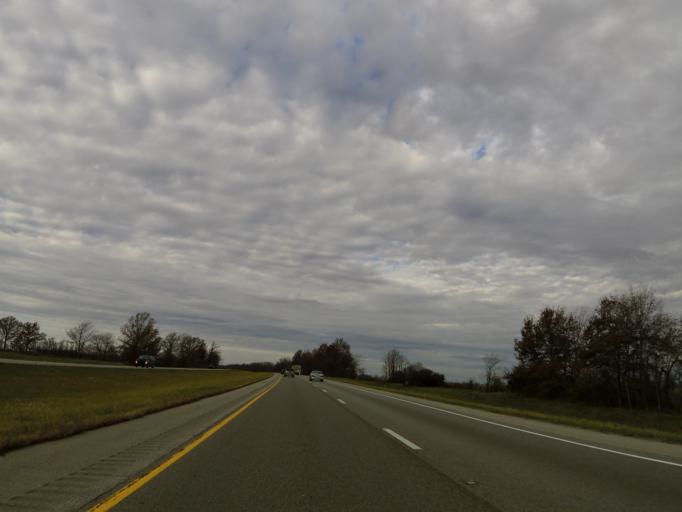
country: US
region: Illinois
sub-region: Clinton County
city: Wamac
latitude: 38.3857
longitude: -89.1273
